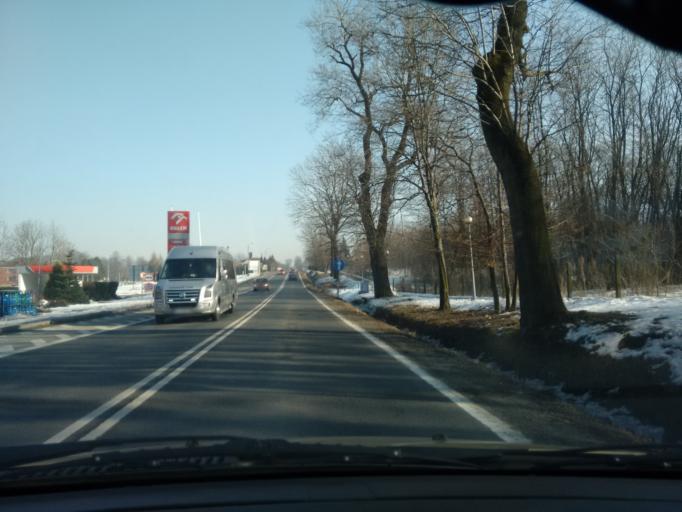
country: PL
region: Silesian Voivodeship
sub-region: Powiat bielski
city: Czaniec
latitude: 49.8799
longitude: 19.2592
